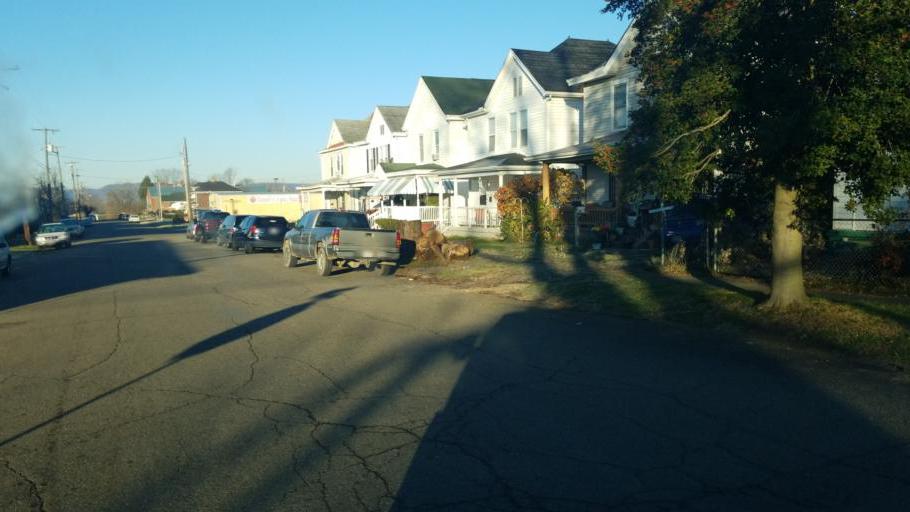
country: US
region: Ohio
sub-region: Scioto County
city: Portsmouth
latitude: 38.7446
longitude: -82.9851
